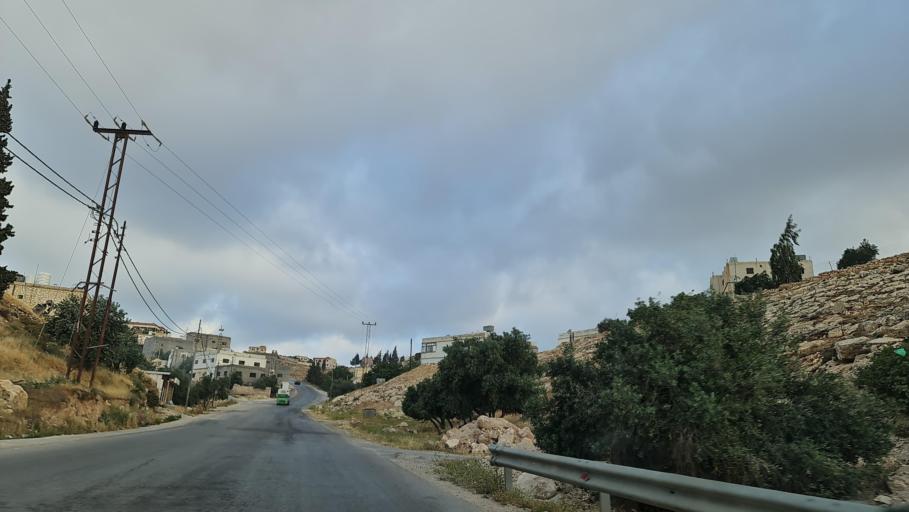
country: JO
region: Amman
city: Al Jubayhah
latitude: 32.0922
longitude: 35.9087
